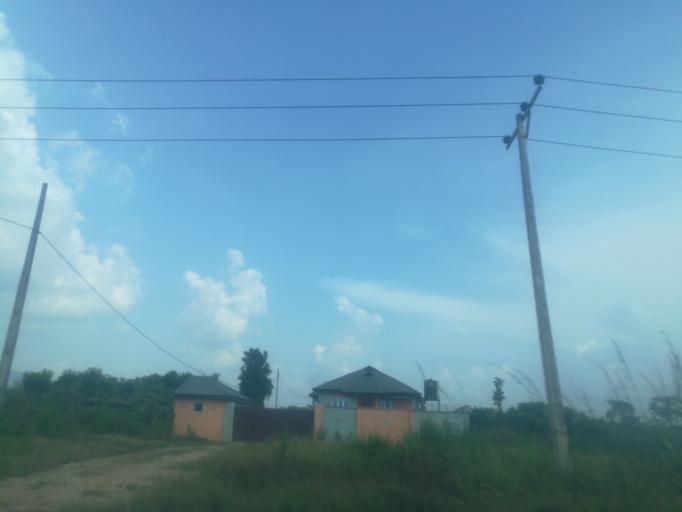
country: NG
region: Ogun
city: Abeokuta
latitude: 7.1046
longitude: 3.2973
